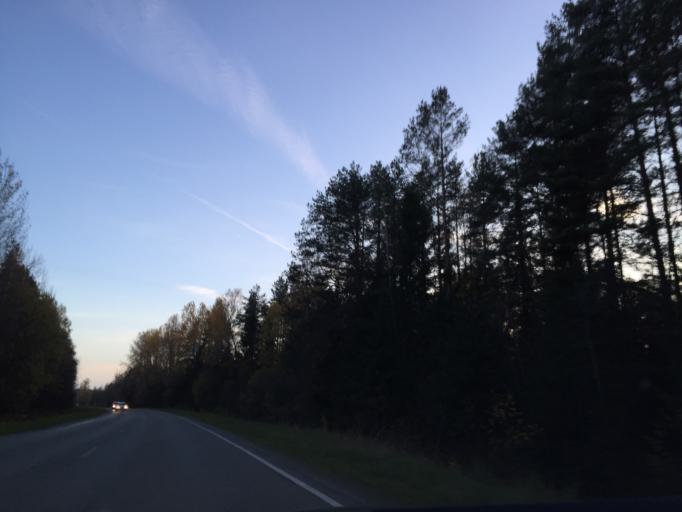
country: LV
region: Malpils
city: Malpils
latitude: 56.8813
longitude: 24.9215
